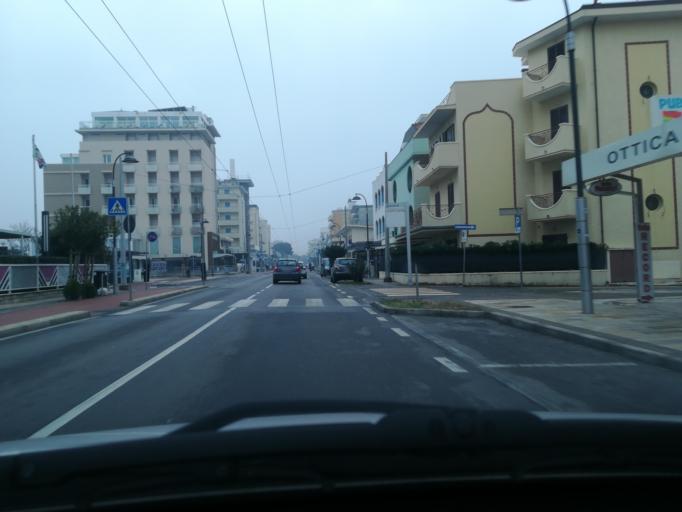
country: IT
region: Emilia-Romagna
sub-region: Provincia di Rimini
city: Riccione
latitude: 44.0153
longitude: 12.6430
